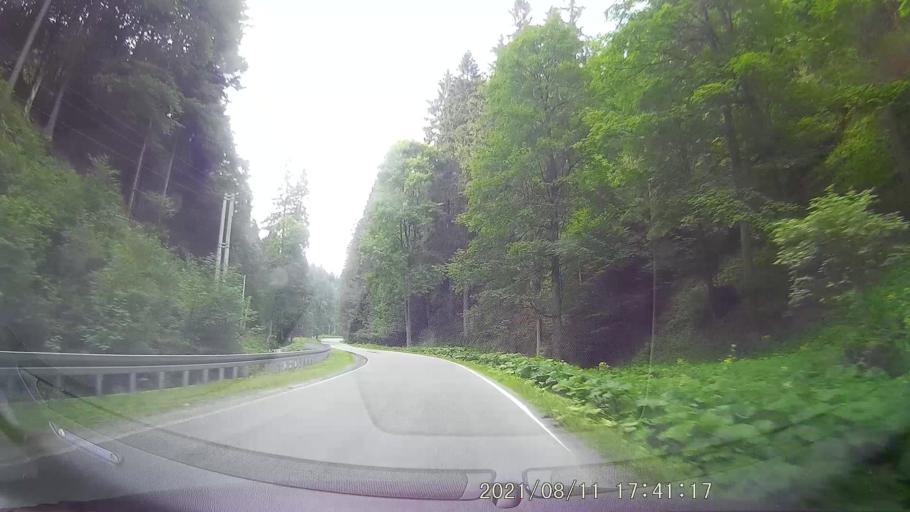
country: PL
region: Lower Silesian Voivodeship
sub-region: Powiat klodzki
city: Duszniki-Zdroj
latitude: 50.3657
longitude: 16.3917
